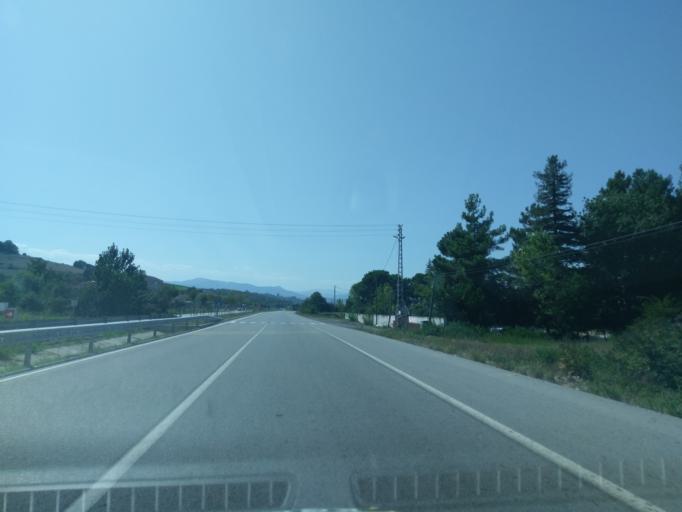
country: TR
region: Samsun
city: Alacam
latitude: 41.6119
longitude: 35.7036
